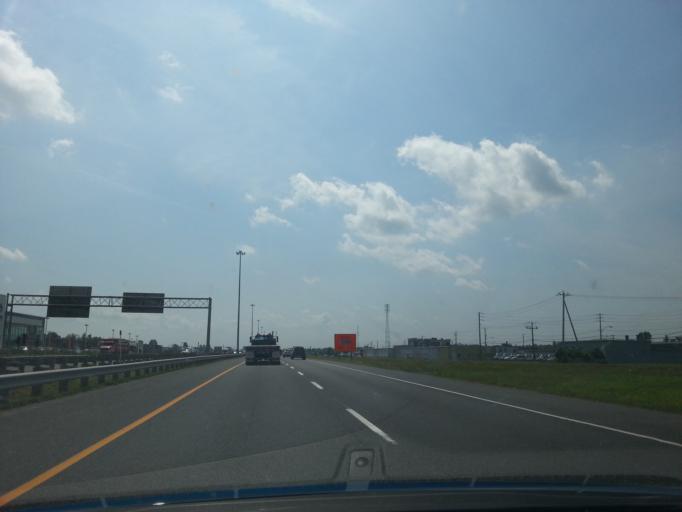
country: CA
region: Quebec
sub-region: Centre-du-Quebec
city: Drummondville
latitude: 45.9000
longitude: -72.5277
